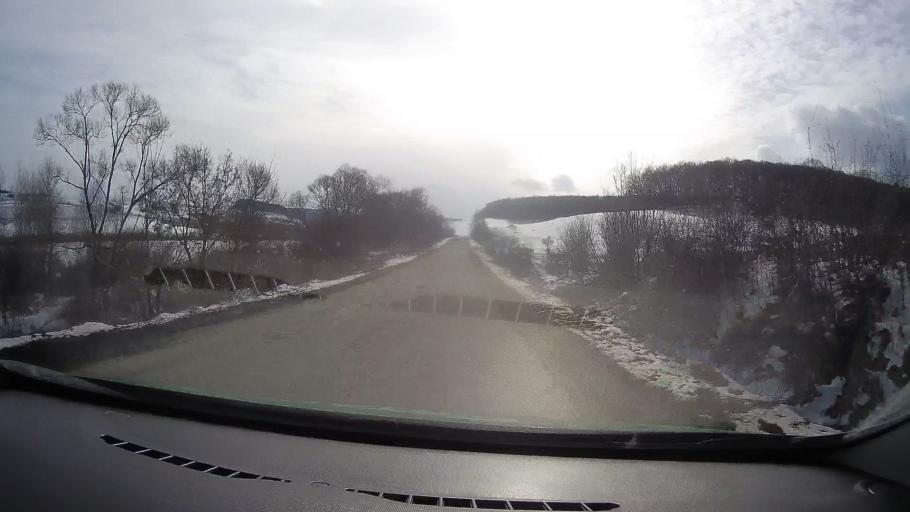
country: RO
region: Sibiu
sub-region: Comuna Bradeni
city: Bradeni
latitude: 46.0953
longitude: 24.8361
